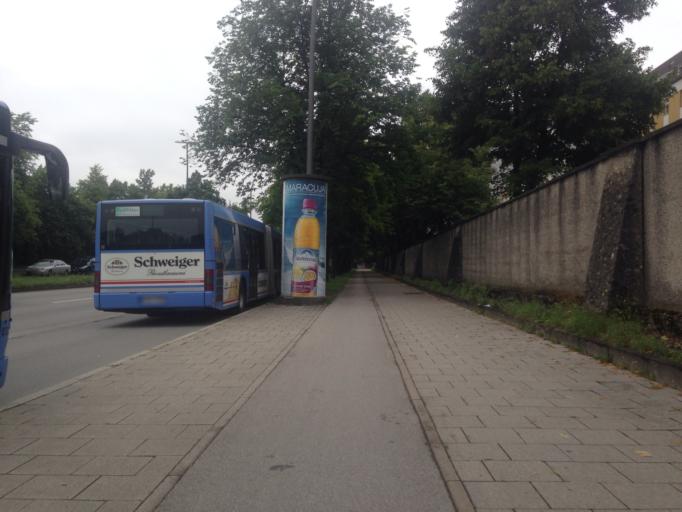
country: DE
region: Bavaria
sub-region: Upper Bavaria
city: Oberschleissheim
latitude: 48.2101
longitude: 11.5869
